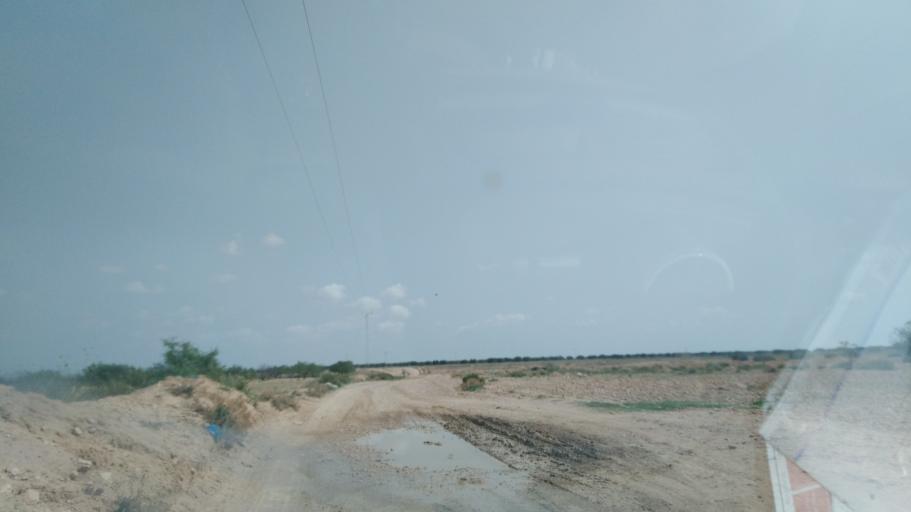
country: TN
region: Safaqis
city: Sfax
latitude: 34.6423
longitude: 10.6187
